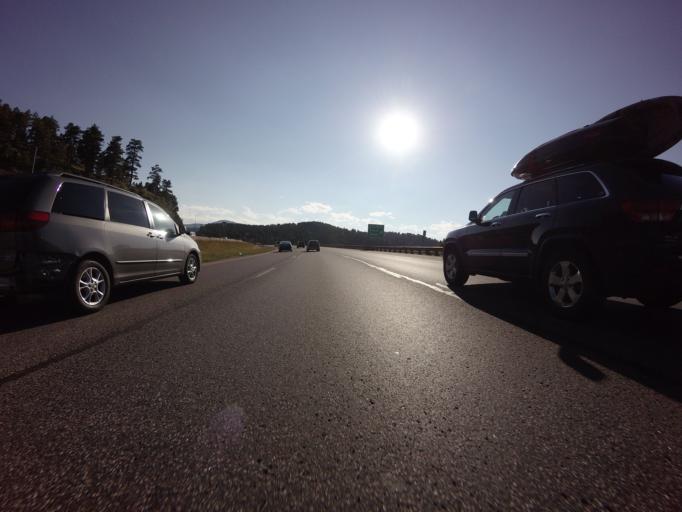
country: US
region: Colorado
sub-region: Jefferson County
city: Genesee
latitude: 39.7142
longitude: -105.3128
